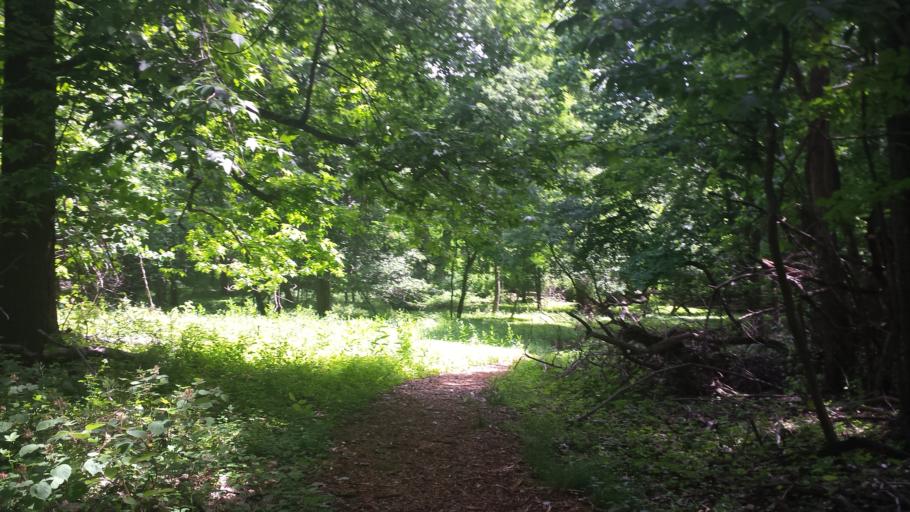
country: US
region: New York
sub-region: Westchester County
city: Harrison
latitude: 40.9559
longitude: -73.7018
